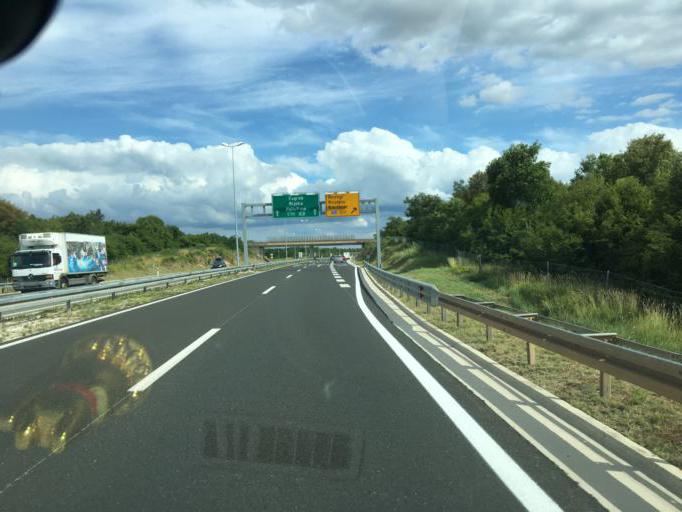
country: HR
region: Istarska
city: Vodnjan
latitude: 45.1173
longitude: 13.8099
